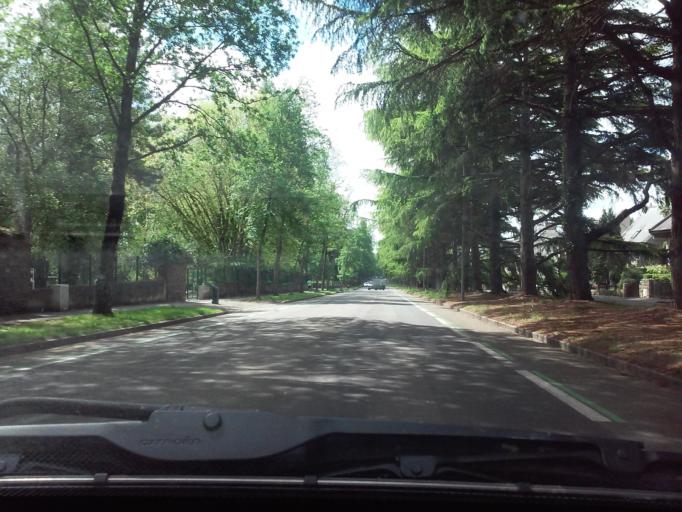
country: FR
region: Brittany
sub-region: Departement d'Ille-et-Vilaine
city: Rennes
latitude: 48.0880
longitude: -1.6914
